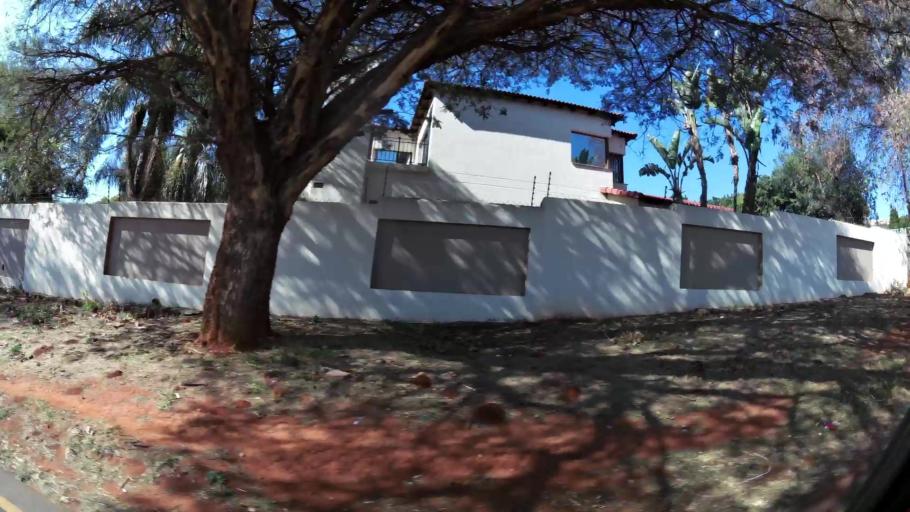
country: ZA
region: Gauteng
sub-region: City of Johannesburg Metropolitan Municipality
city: Roodepoort
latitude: -26.1355
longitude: 27.9124
